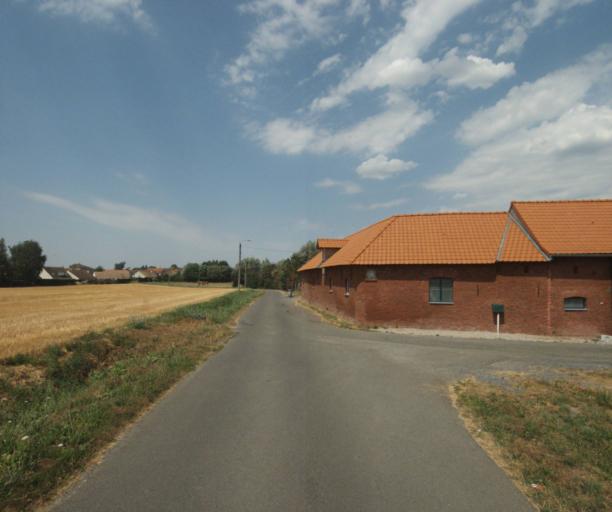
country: FR
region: Nord-Pas-de-Calais
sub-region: Departement du Nord
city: Comines
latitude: 50.7636
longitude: 3.0273
